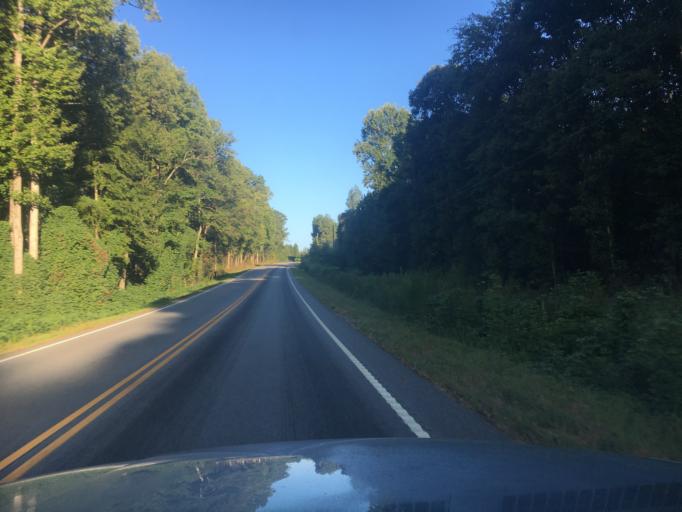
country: US
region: South Carolina
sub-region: Spartanburg County
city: Woodruff
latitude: 34.7002
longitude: -81.9494
